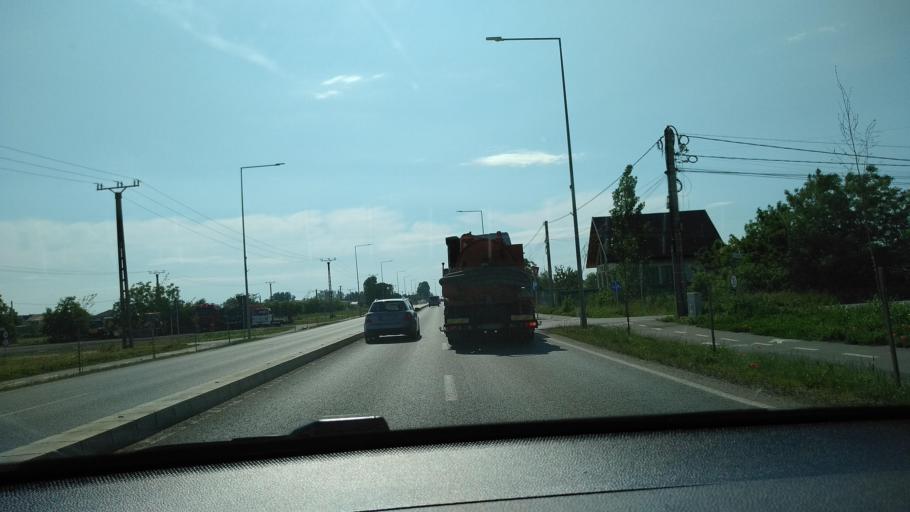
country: RO
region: Timis
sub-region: Comuna Mosnita Noua
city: Mosnita Noua
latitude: 45.7219
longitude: 21.3053
